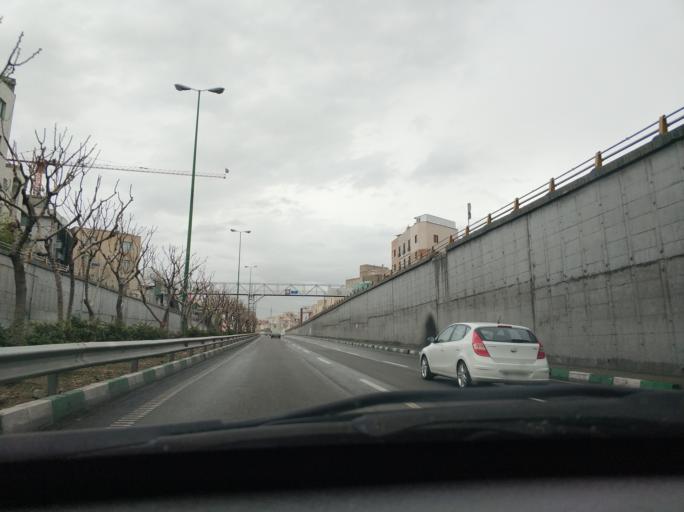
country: IR
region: Tehran
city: Tehran
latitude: 35.7228
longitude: 51.4523
